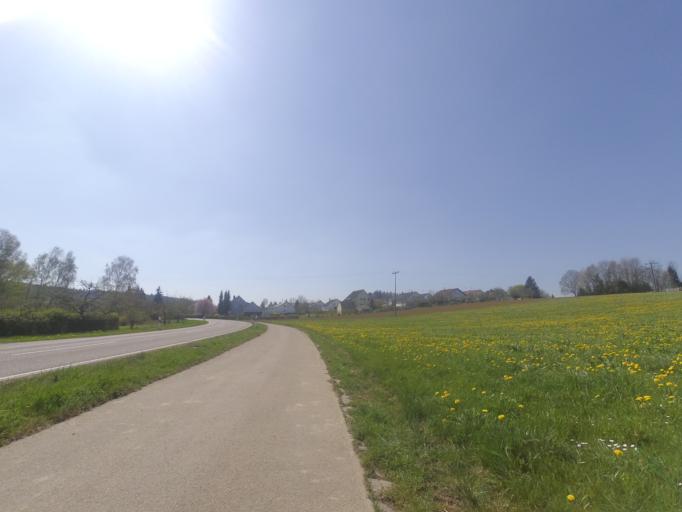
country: DE
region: Bavaria
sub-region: Swabia
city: Roggenburg
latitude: 48.3159
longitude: 10.2100
